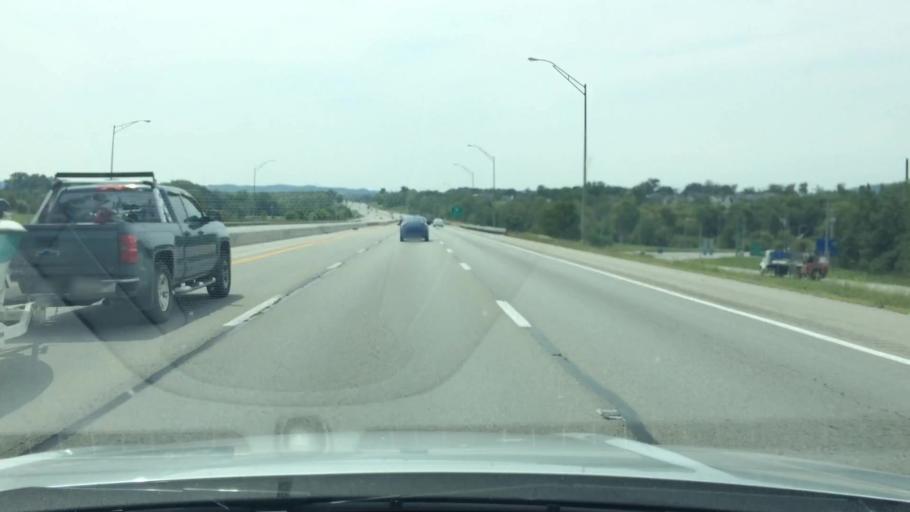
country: US
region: Kentucky
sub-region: Madison County
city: Berea
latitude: 37.5995
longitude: -84.3139
